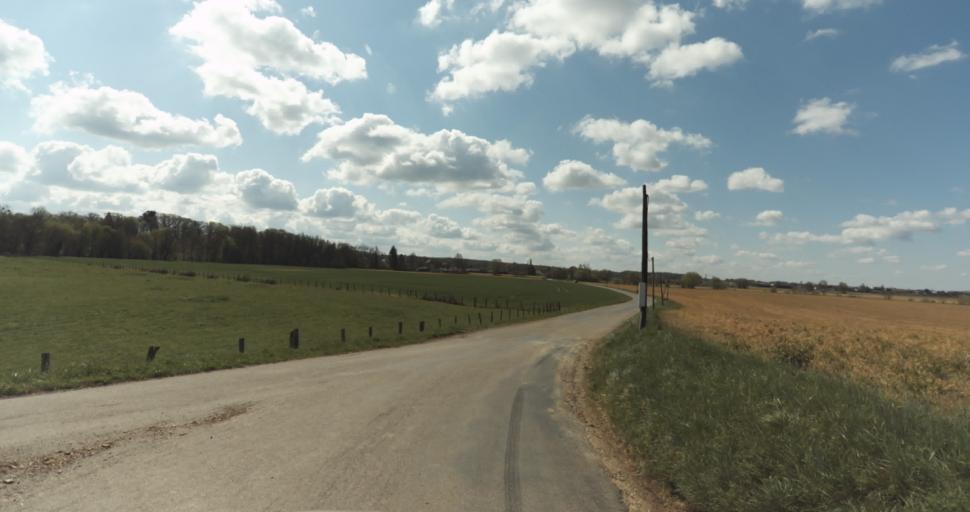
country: FR
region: Bourgogne
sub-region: Departement de la Cote-d'Or
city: Auxonne
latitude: 47.2066
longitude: 5.4240
